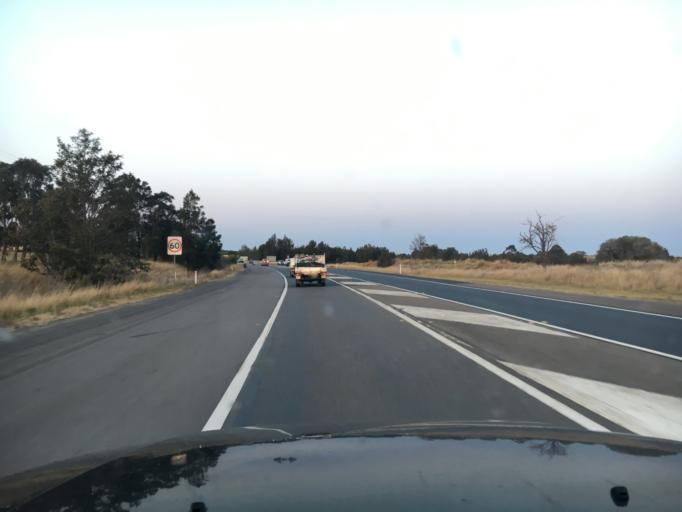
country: AU
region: New South Wales
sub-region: Cessnock
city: Greta
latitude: -32.7037
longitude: 151.4407
